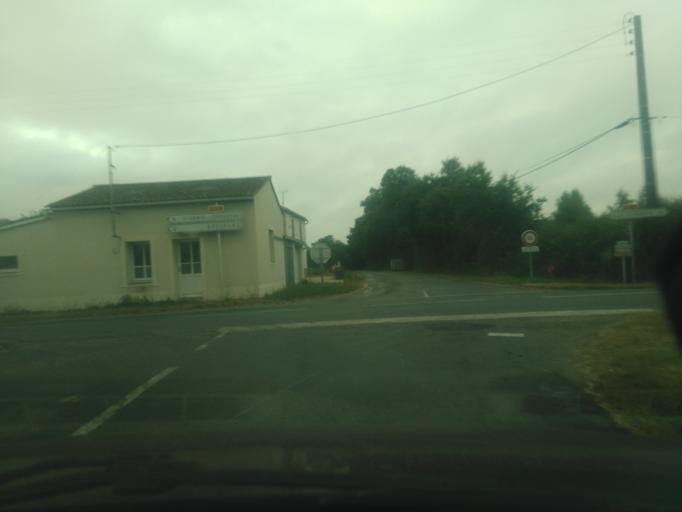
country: FR
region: Pays de la Loire
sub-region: Departement de la Vendee
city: Chauche
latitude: 46.7863
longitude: -1.3018
